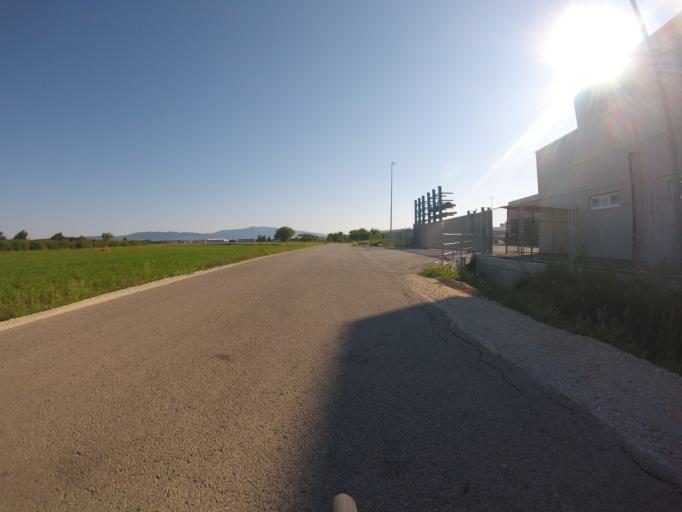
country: HR
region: Grad Zagreb
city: Lucko
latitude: 45.7472
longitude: 15.8716
